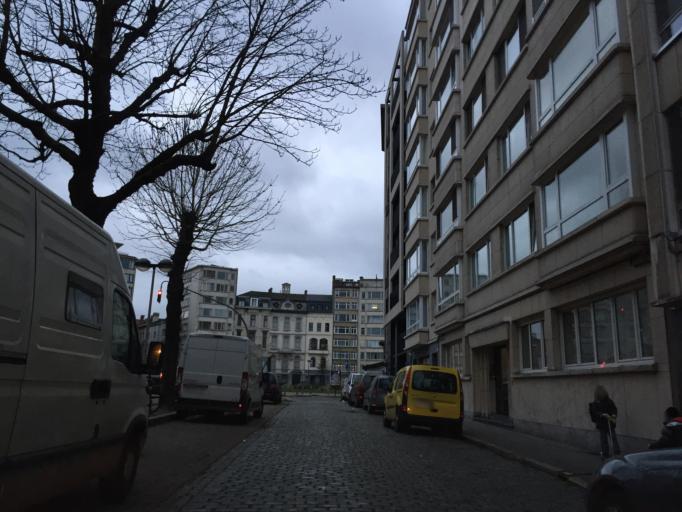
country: BE
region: Flanders
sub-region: Provincie Antwerpen
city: Antwerpen
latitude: 51.2076
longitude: 4.4190
